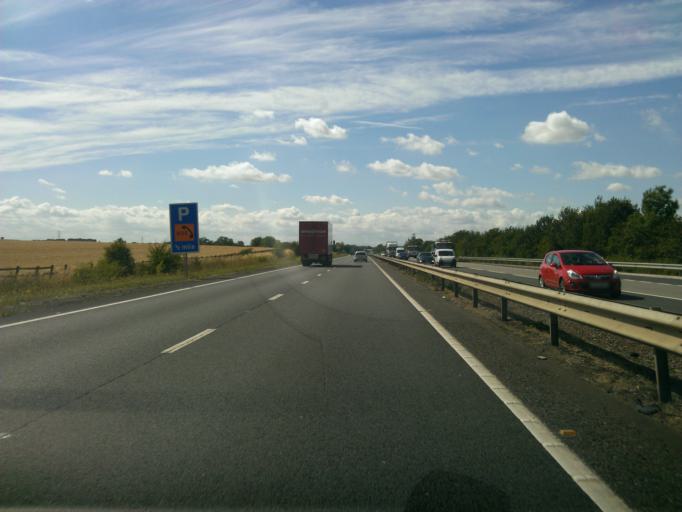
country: GB
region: England
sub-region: Bedford
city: Pertenhall
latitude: 52.3628
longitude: -0.4222
